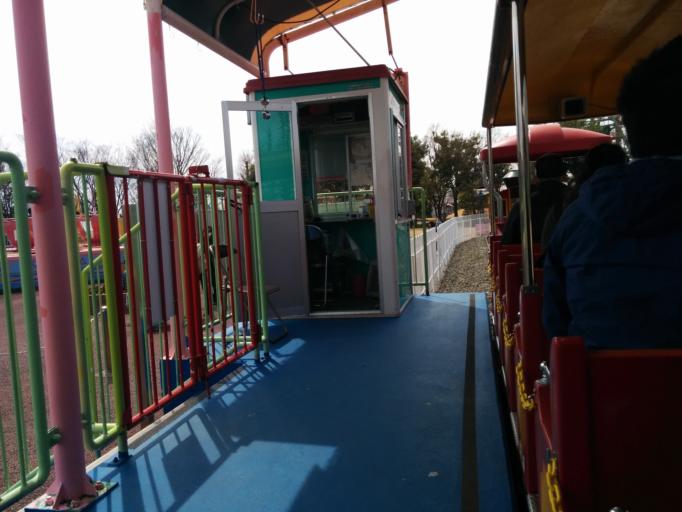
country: JP
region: Fukushima
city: Koriyama
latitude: 37.3677
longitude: 140.3284
